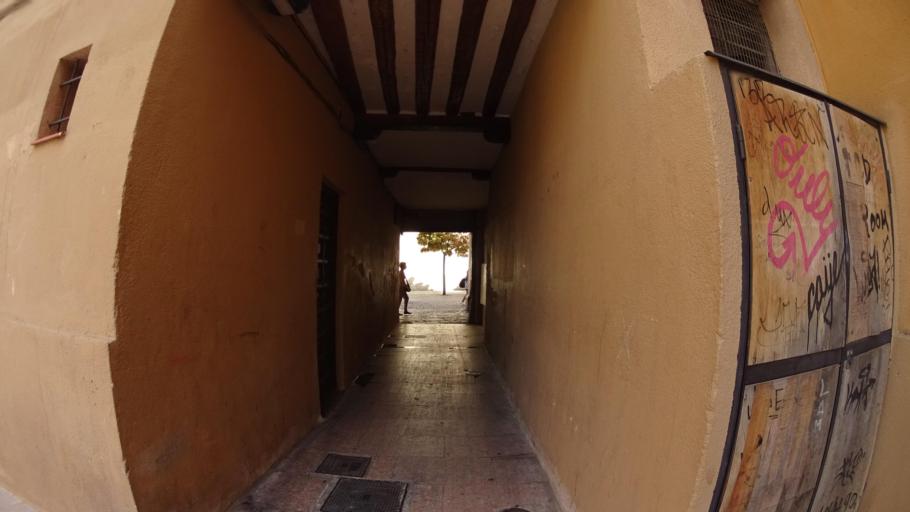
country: ES
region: Madrid
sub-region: Provincia de Madrid
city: Alcala de Henares
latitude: 40.4820
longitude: -3.3666
